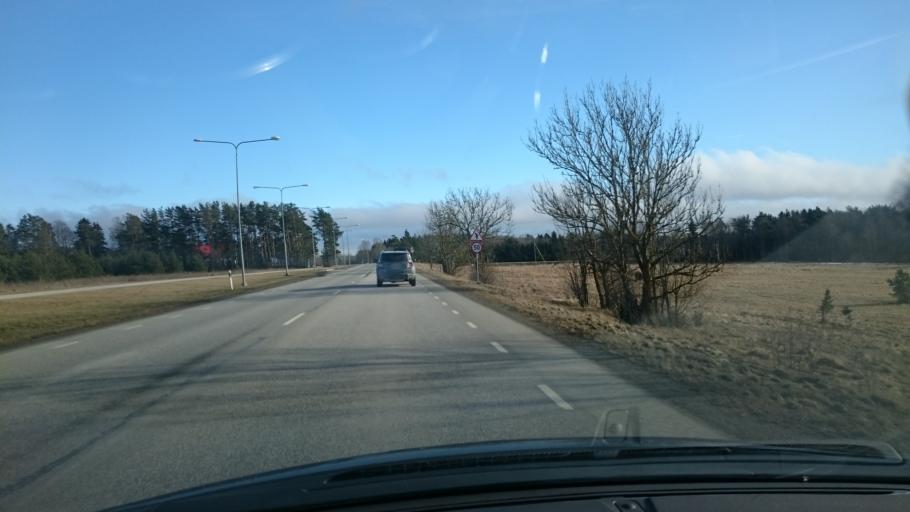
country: EE
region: Harju
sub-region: Harku vald
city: Tabasalu
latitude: 59.4398
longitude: 24.4968
